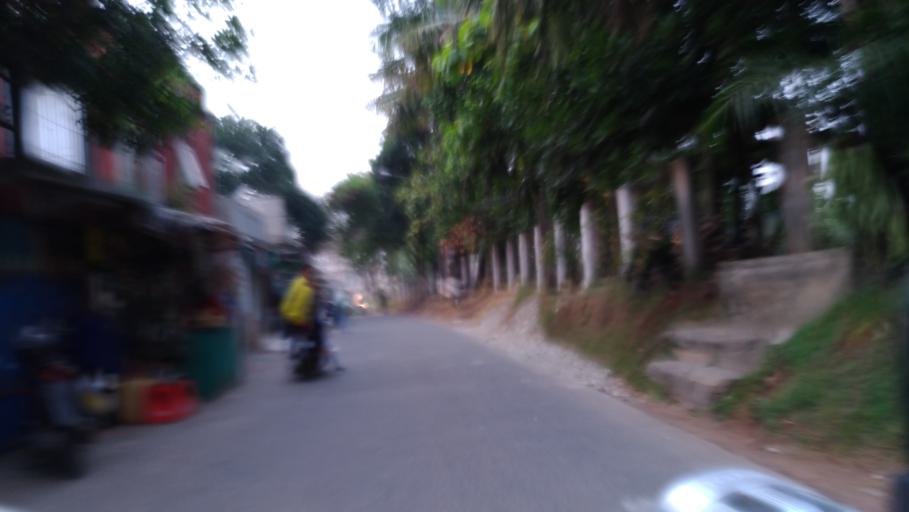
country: ID
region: West Java
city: Depok
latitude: -6.3594
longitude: 106.8698
